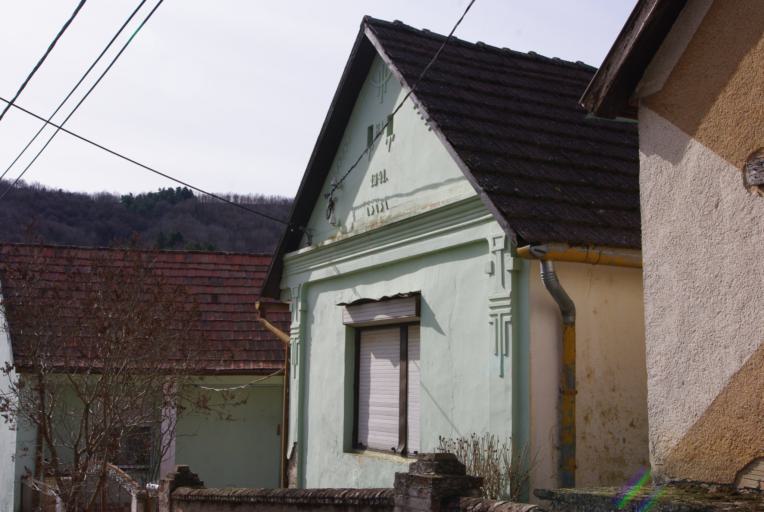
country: HU
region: Baranya
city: Villany
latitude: 45.8810
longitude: 18.4249
